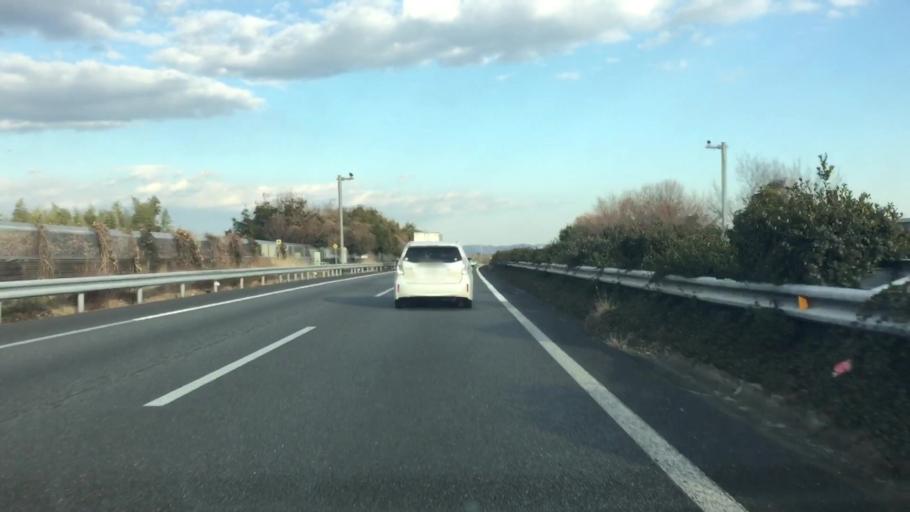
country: JP
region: Gunma
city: Isesaki
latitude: 36.3553
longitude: 139.1955
